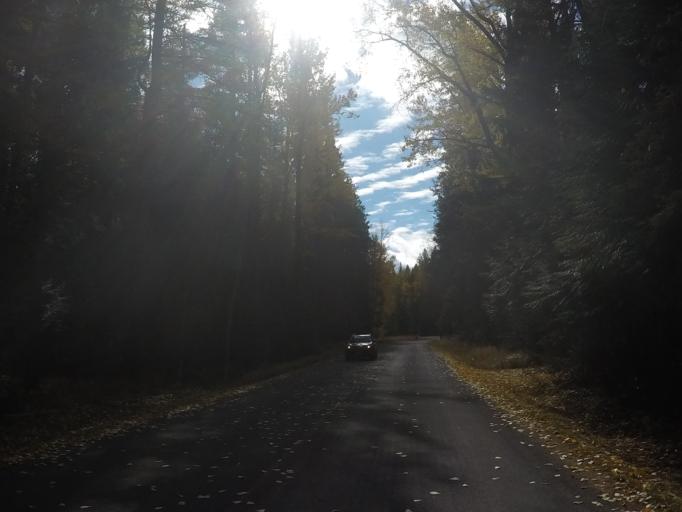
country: US
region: Montana
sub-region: Flathead County
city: Columbia Falls
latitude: 48.5257
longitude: -113.9940
